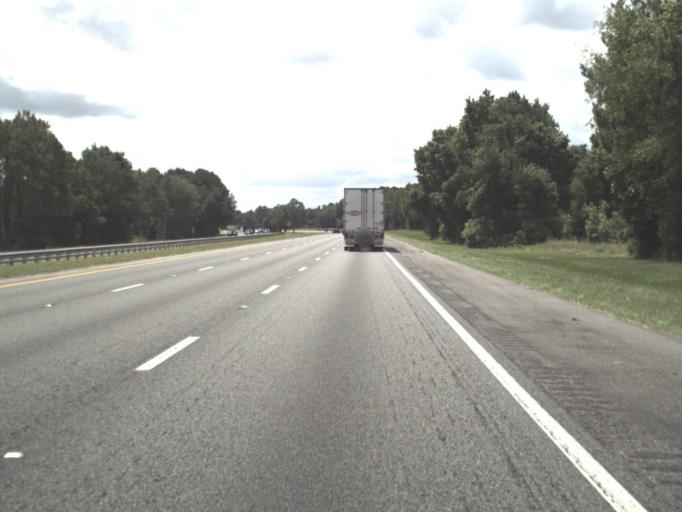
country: US
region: Florida
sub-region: Suwannee County
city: Wellborn
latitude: 30.2456
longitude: -82.7427
